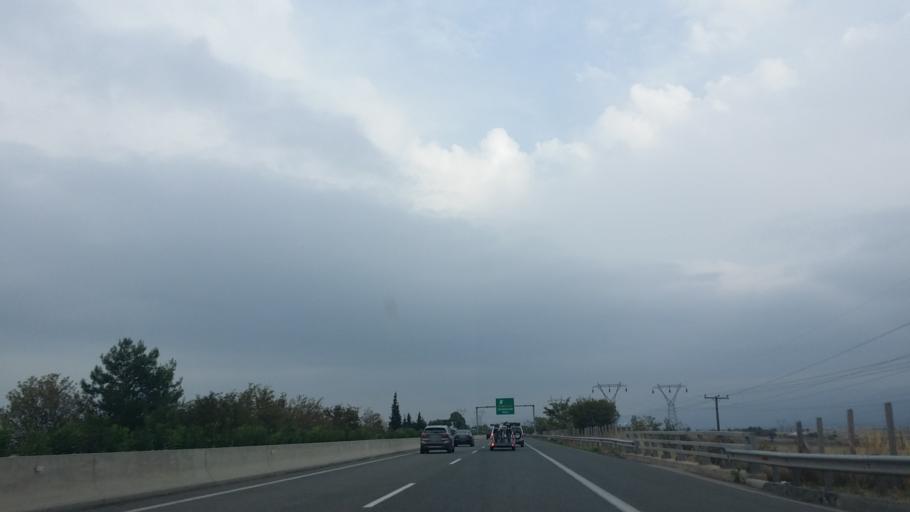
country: GR
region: Central Greece
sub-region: Nomos Voiotias
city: Schimatari
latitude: 38.3615
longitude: 23.5527
